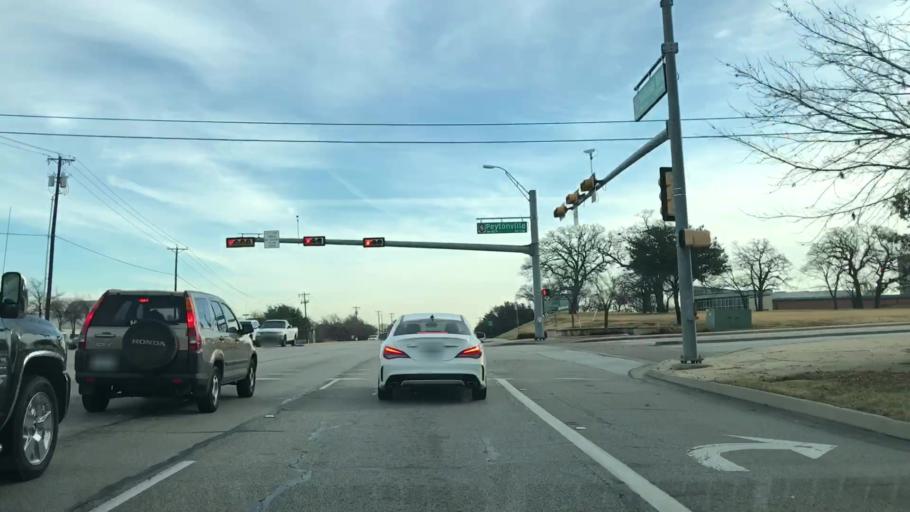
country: US
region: Texas
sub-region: Tarrant County
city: Southlake
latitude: 32.9413
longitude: -97.1775
